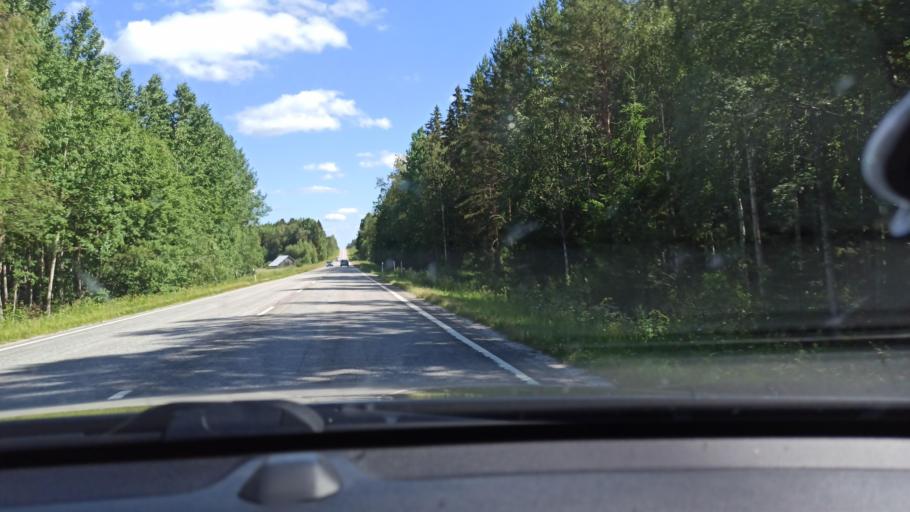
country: FI
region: Ostrobothnia
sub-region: Vaasa
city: Malax
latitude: 62.9905
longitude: 21.6447
